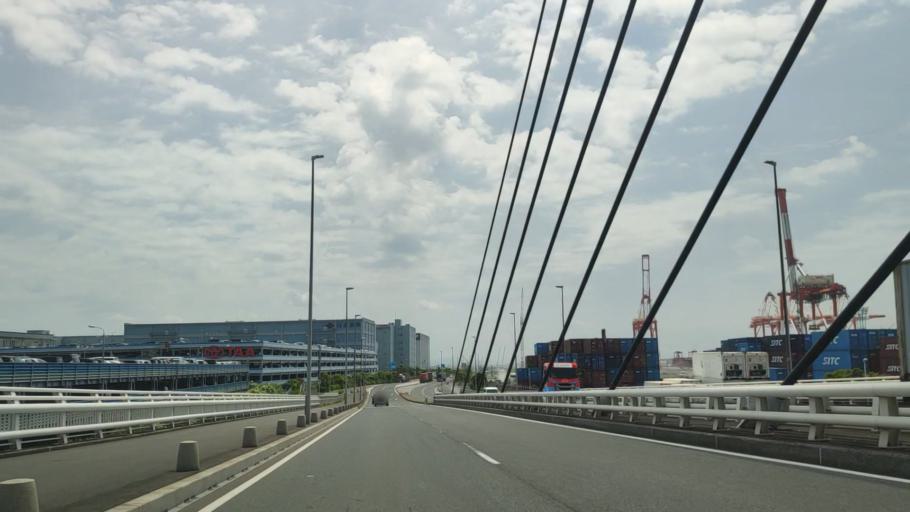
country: JP
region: Kanagawa
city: Yokohama
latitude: 35.4088
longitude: 139.6795
